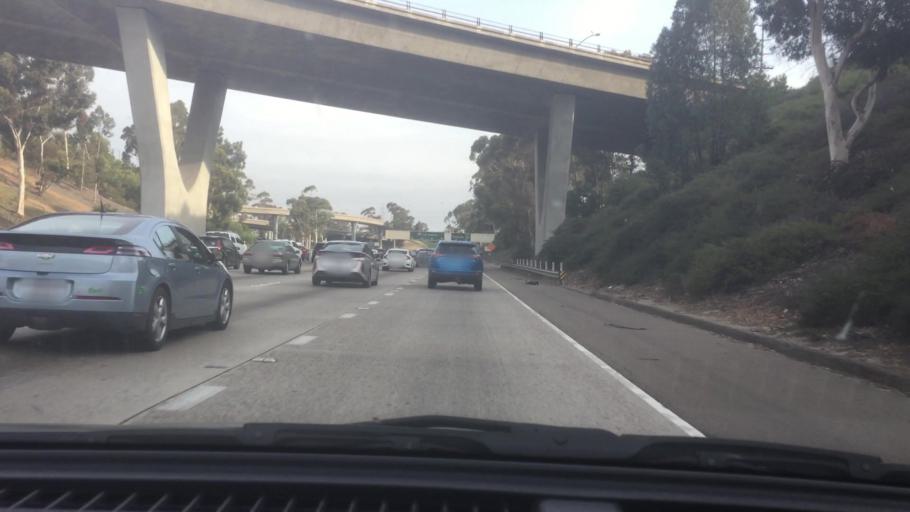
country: US
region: California
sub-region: San Diego County
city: San Diego
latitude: 32.8033
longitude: -117.1504
